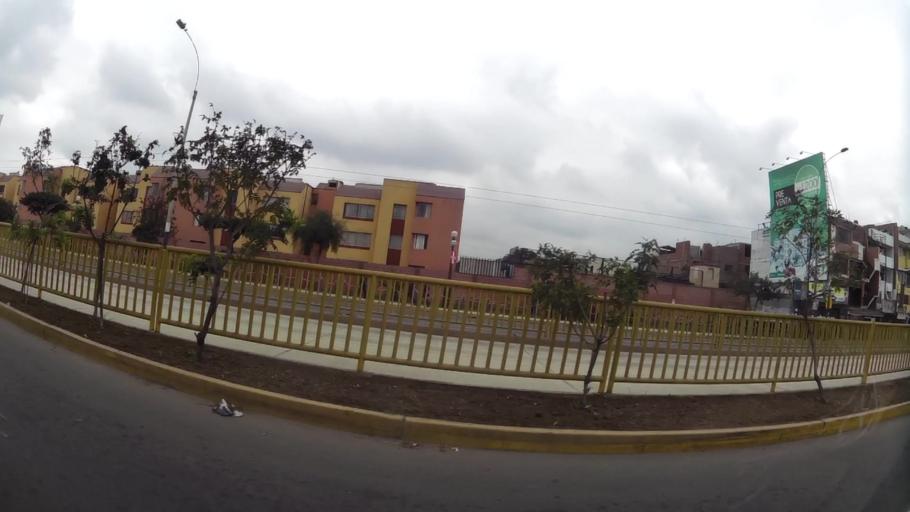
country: PE
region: Lima
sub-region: Lima
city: Surco
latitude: -12.1762
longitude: -77.0124
